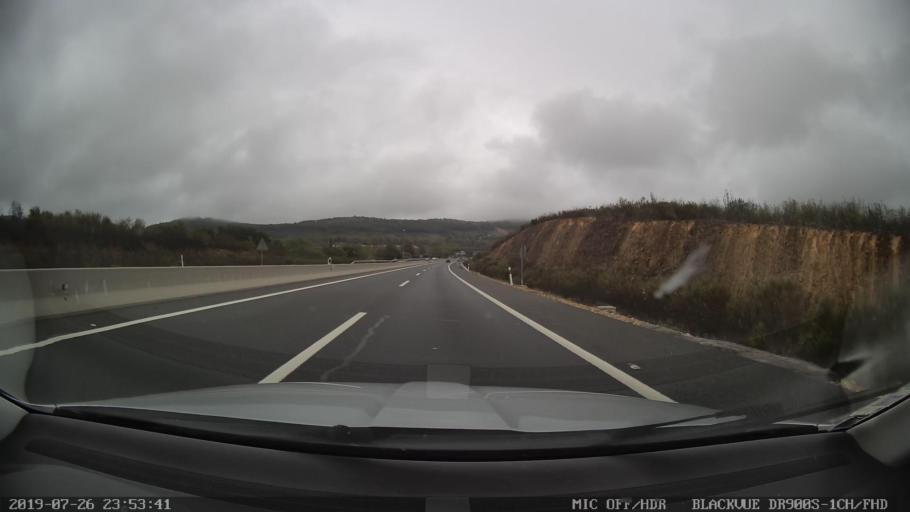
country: ES
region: Extremadura
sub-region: Provincia de Caceres
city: Casas de Miravete
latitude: 39.6854
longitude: -5.7209
